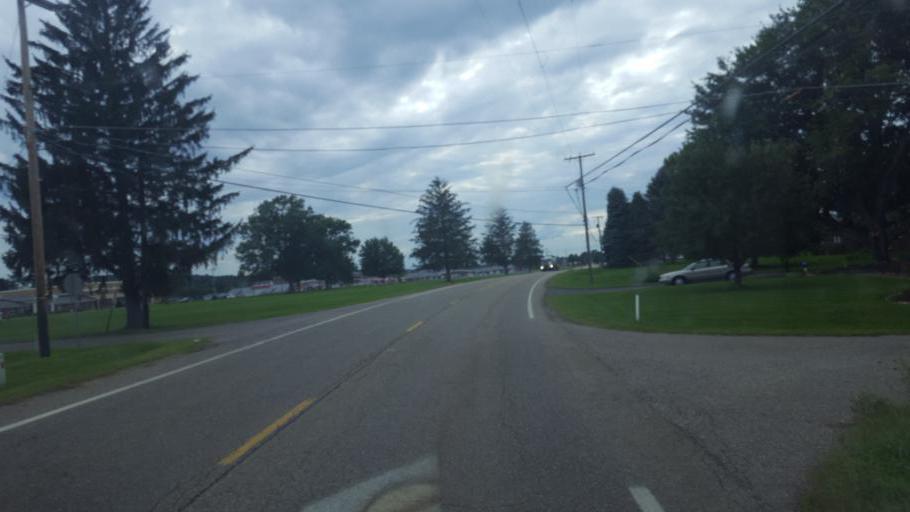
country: US
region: Ohio
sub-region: Carroll County
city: Lake Mohawk
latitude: 40.6389
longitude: -81.3462
